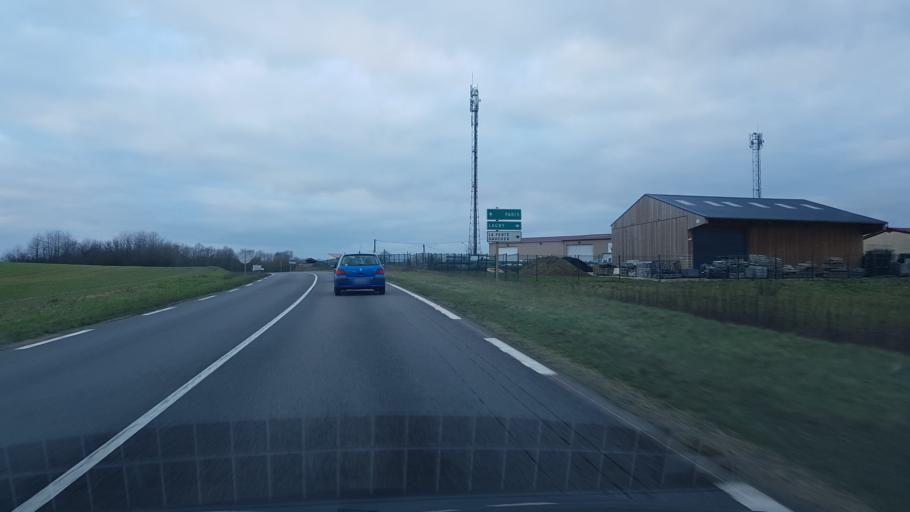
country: FR
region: Champagne-Ardenne
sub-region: Departement de la Marne
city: Esternay
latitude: 48.7191
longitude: 3.5418
